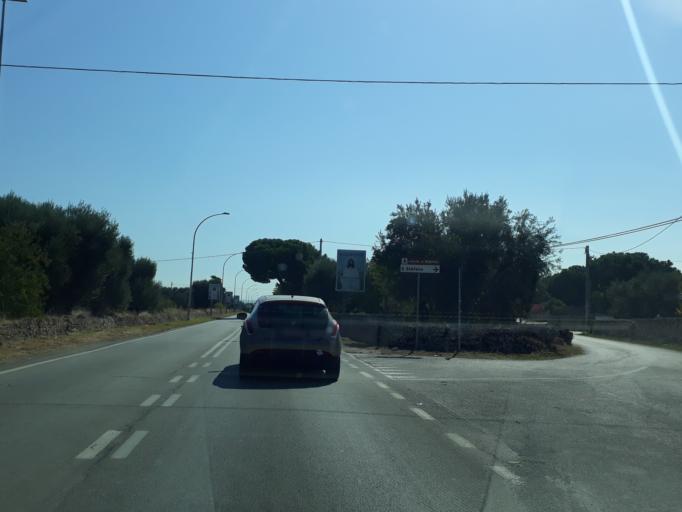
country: IT
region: Apulia
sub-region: Provincia di Bari
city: Monopoli
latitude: 40.9311
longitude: 17.3117
